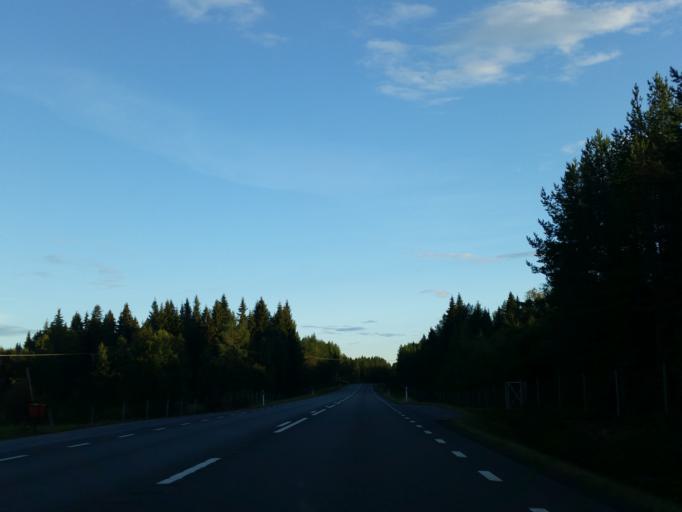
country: SE
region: Vaesterbotten
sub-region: Robertsfors Kommun
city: Robertsfors
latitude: 64.0286
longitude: 20.8414
